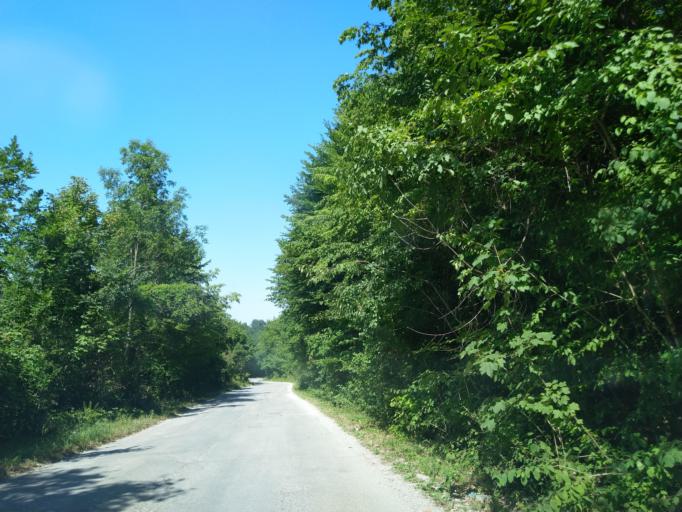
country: RS
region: Central Serbia
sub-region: Zlatiborski Okrug
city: Uzice
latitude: 43.8179
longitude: 19.8560
